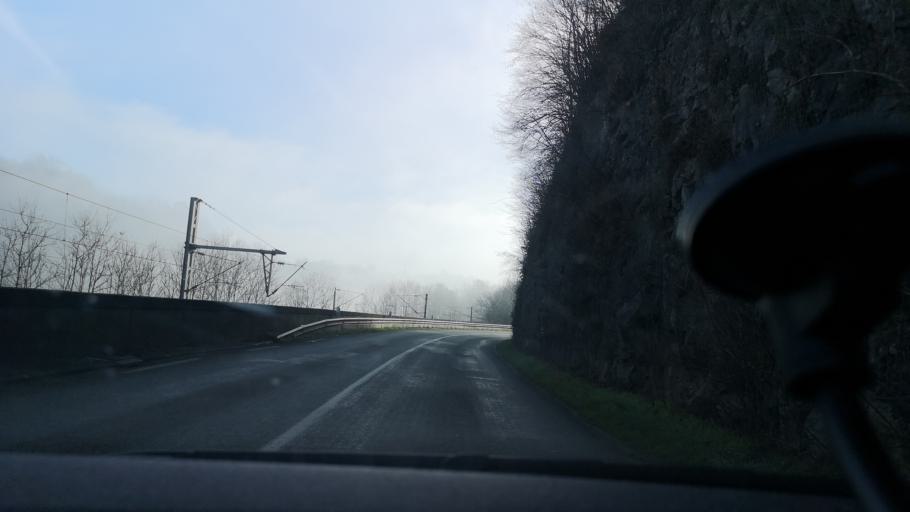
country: FR
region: Franche-Comte
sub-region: Departement du Doubs
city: Clerval
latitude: 47.3872
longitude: 6.4988
